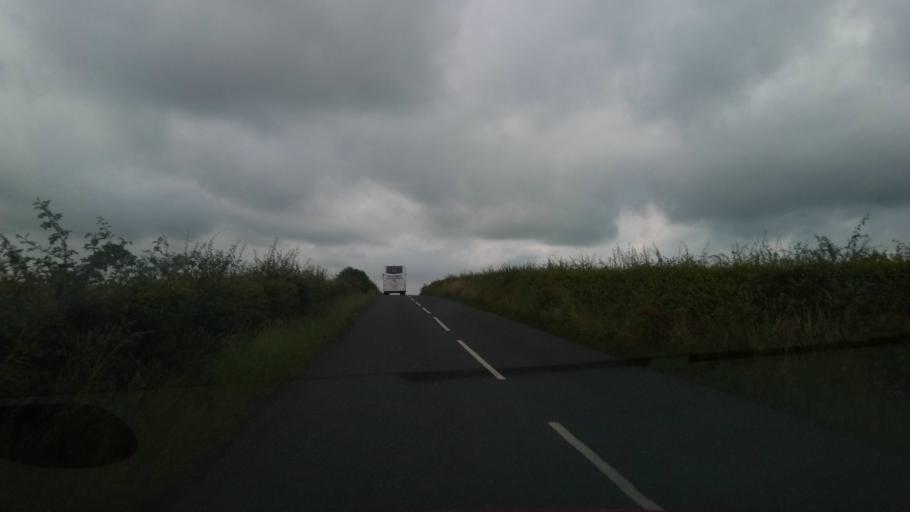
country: GB
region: Scotland
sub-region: Dumfries and Galloway
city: Langholm
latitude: 55.0940
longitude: -2.9012
